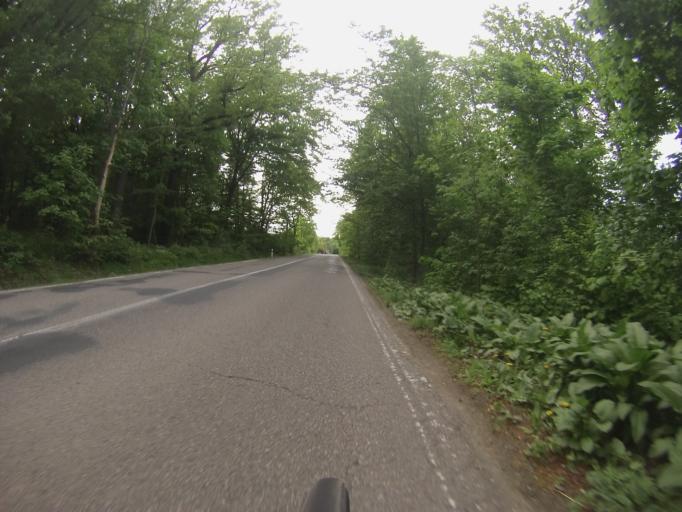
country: CZ
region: South Moravian
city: Veverska Bityska
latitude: 49.2542
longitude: 16.4786
